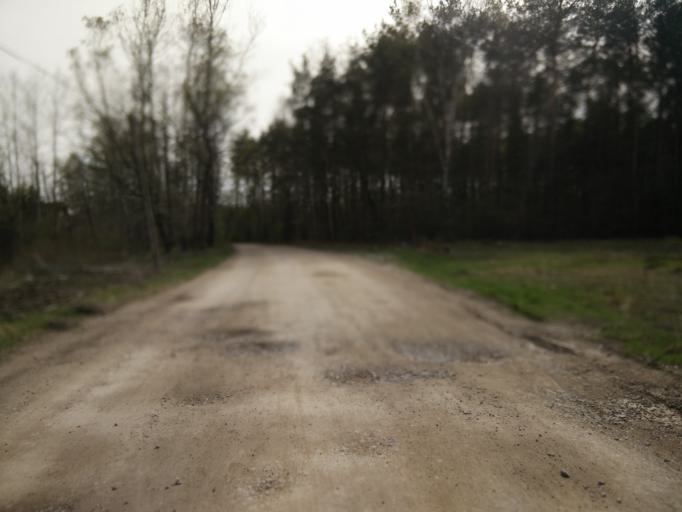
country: PL
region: Masovian Voivodeship
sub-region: Powiat warszawski zachodni
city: Izabelin
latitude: 52.2888
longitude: 20.8391
